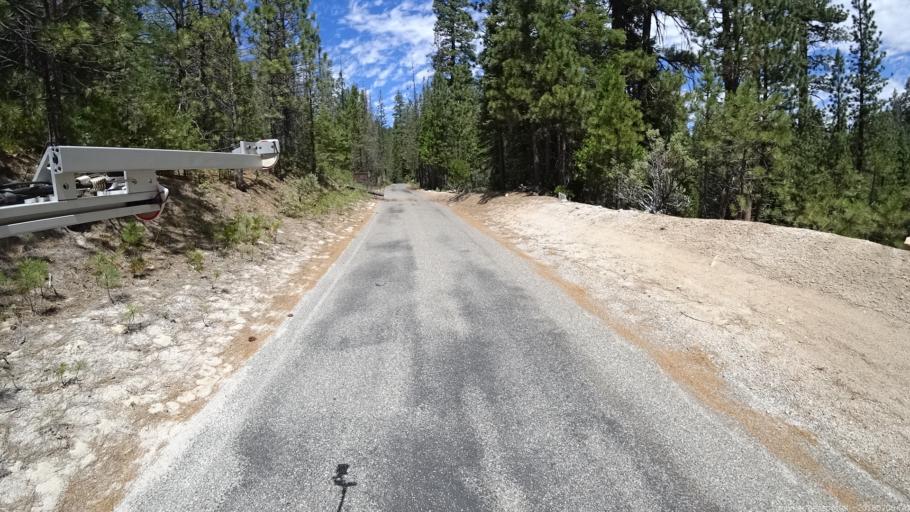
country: US
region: California
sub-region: Madera County
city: Oakhurst
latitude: 37.4048
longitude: -119.3946
